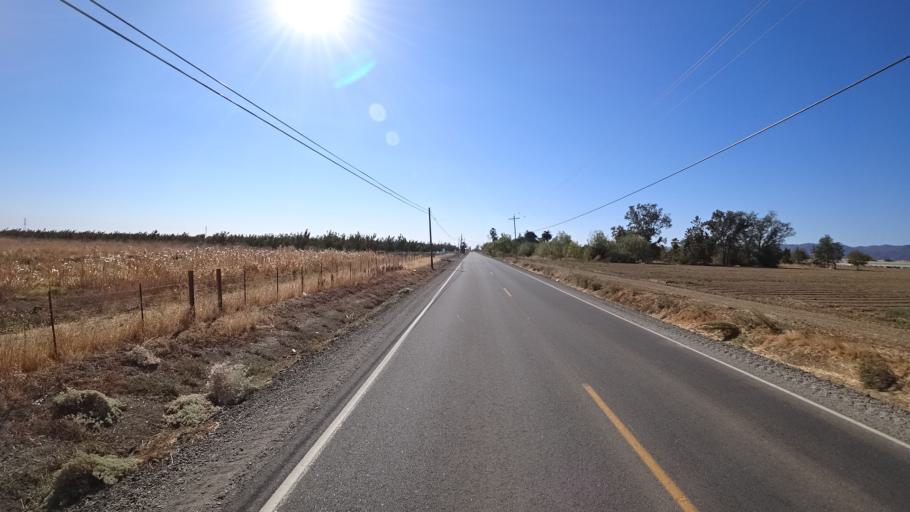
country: US
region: California
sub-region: Yolo County
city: Cottonwood
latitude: 38.6263
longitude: -121.9714
